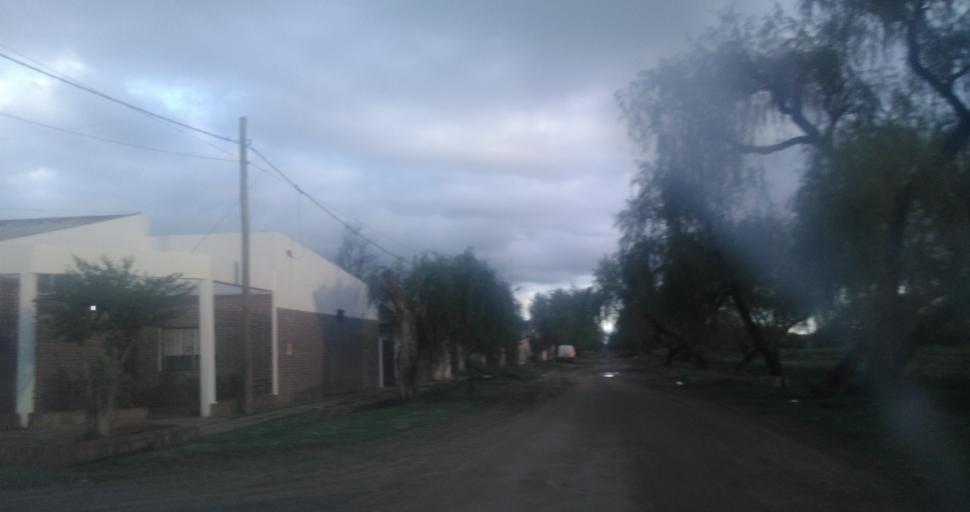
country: AR
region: Chaco
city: Resistencia
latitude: -27.4695
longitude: -58.9744
